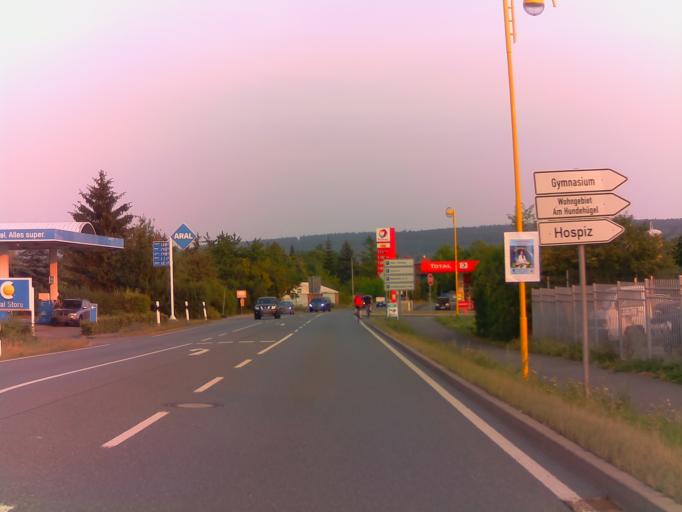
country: DE
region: Thuringia
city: Bad Berka
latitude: 50.9050
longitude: 11.2774
